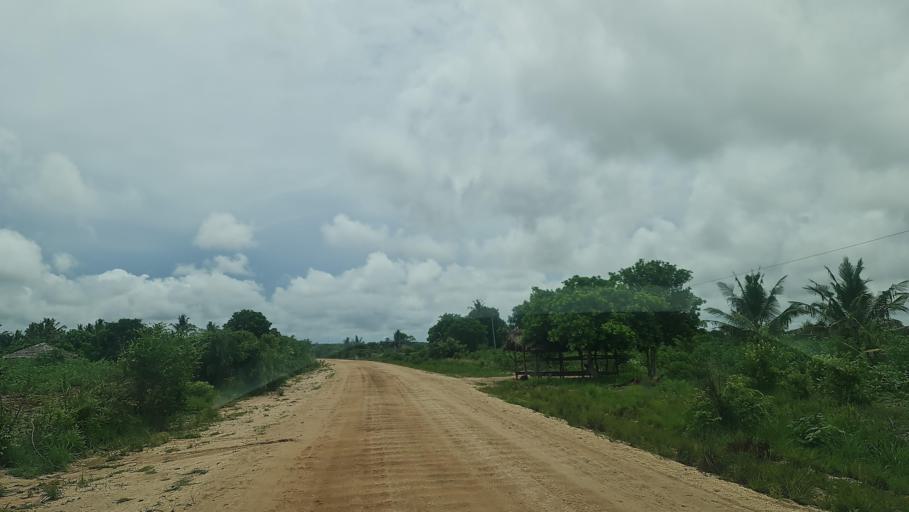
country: MZ
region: Zambezia
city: Quelimane
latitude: -17.2663
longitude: 37.2421
